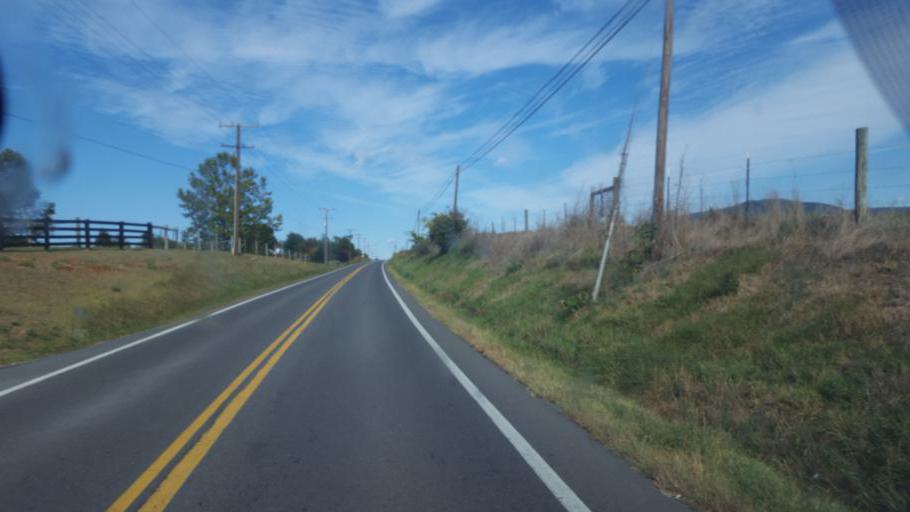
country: US
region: Virginia
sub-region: Page County
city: Luray
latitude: 38.7053
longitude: -78.4400
